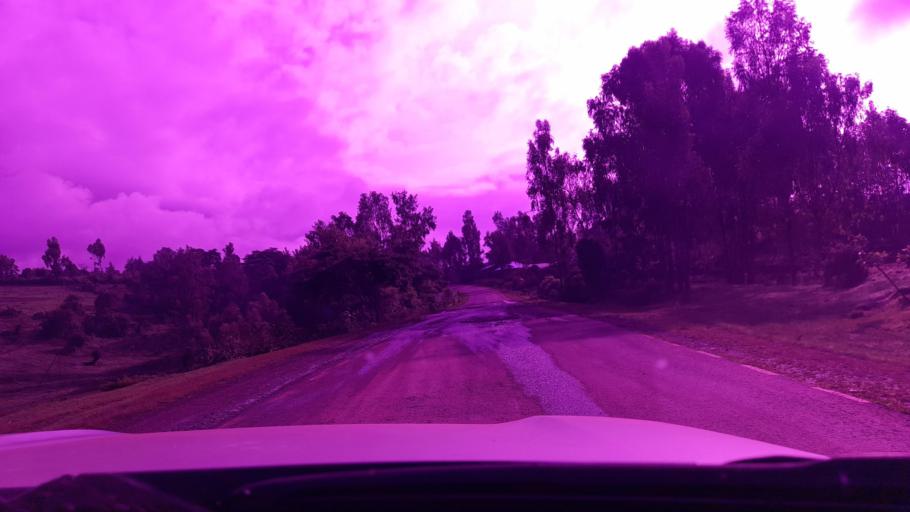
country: ET
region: Oromiya
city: Bedele
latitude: 8.2193
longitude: 36.4459
